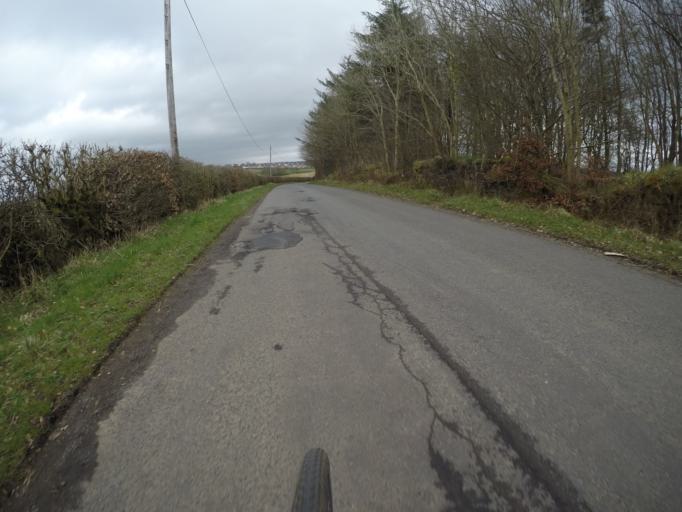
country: GB
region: Scotland
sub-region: East Ayrshire
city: Stewarton
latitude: 55.6779
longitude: -4.5406
